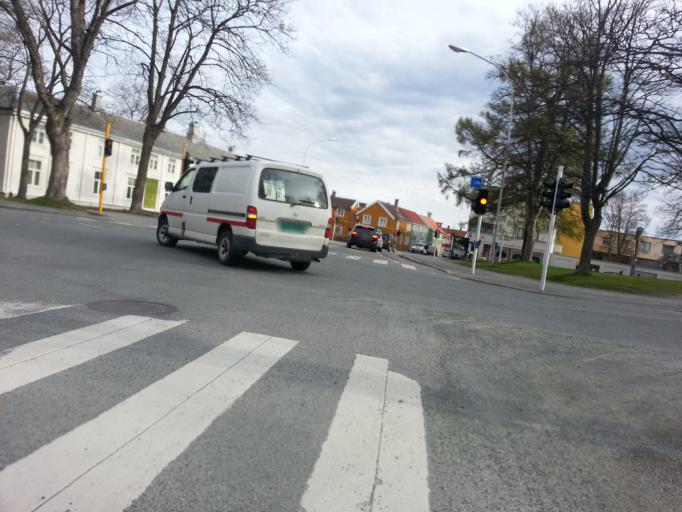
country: NO
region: Sor-Trondelag
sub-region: Trondheim
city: Trondheim
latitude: 63.4212
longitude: 10.3987
